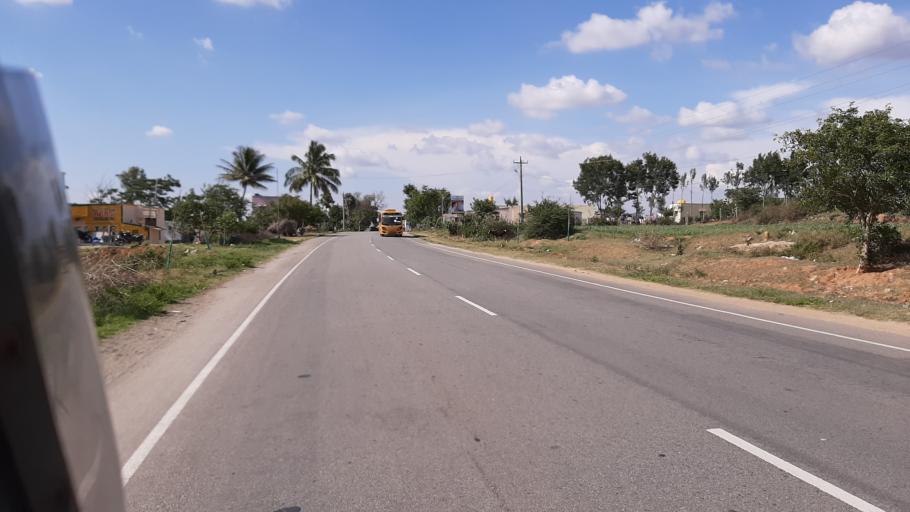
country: IN
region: Tamil Nadu
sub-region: Krishnagiri
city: Denkanikota
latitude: 12.5536
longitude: 77.7854
